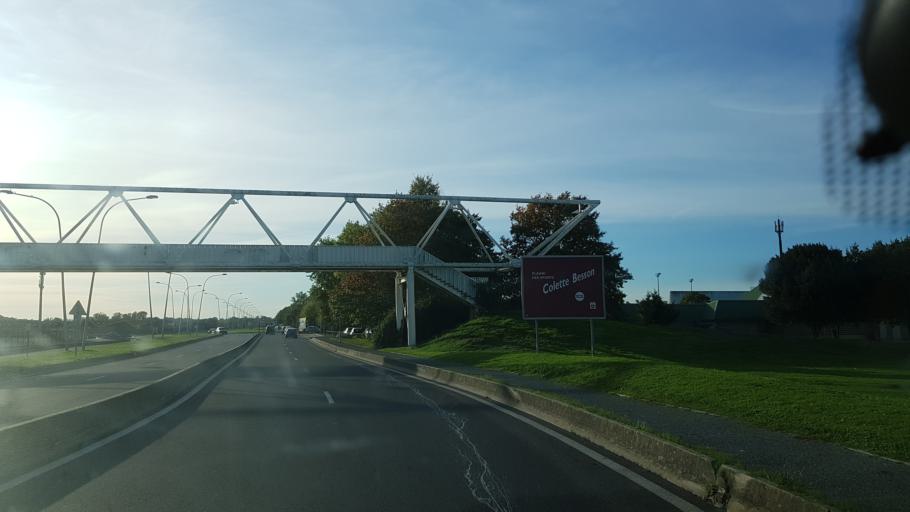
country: FR
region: Aquitaine
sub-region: Departement de la Gironde
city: Le Bouscat
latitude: 44.8983
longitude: -0.5660
